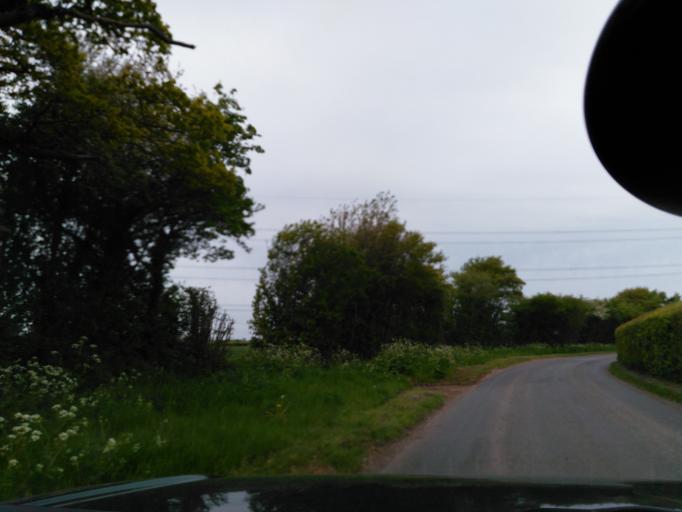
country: GB
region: England
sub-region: Wiltshire
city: Lacock
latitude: 51.4242
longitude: -2.1412
